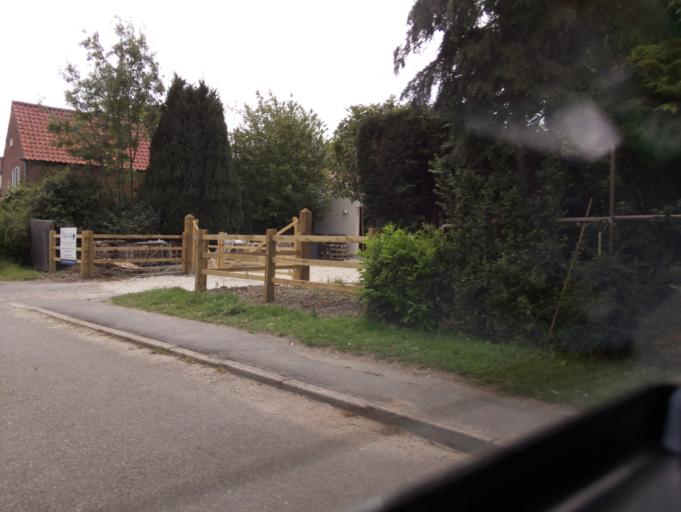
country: GB
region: England
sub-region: Nottinghamshire
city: Cotgrave
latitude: 52.8690
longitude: -1.0680
